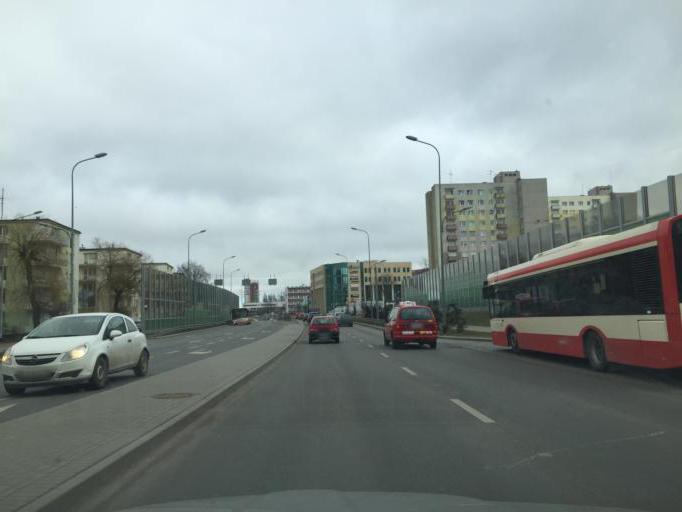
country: PL
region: Pomeranian Voivodeship
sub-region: Sopot
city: Sopot
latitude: 54.3781
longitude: 18.5807
